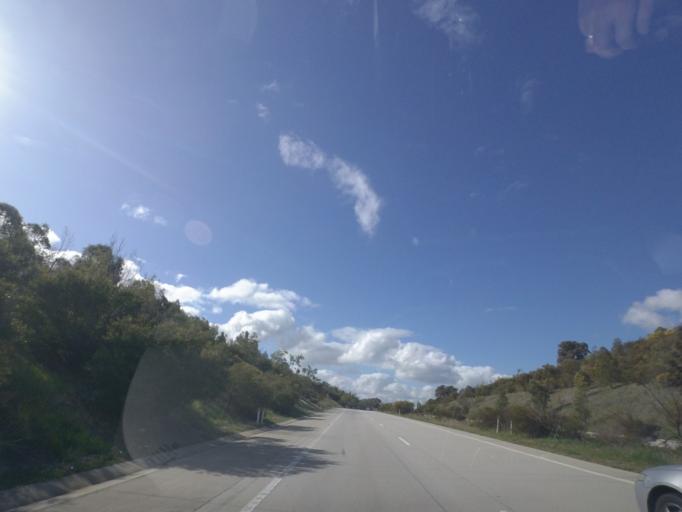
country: AU
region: New South Wales
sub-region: Albury Municipality
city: Lavington
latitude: -35.9200
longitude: 147.0952
